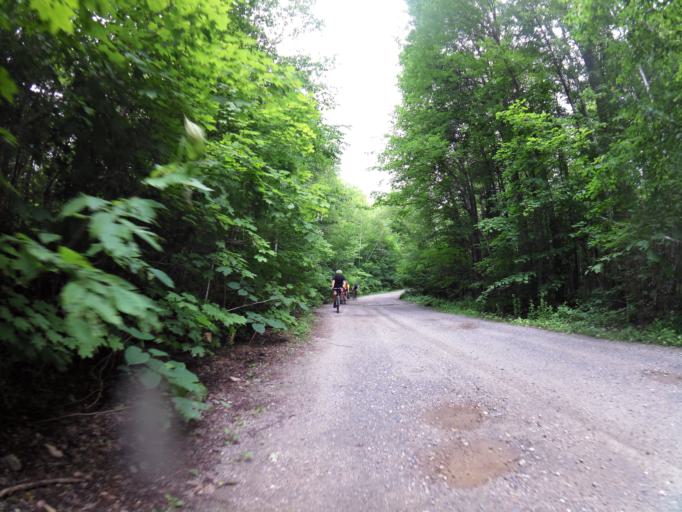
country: CA
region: Ontario
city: Perth
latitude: 45.0206
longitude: -76.5797
